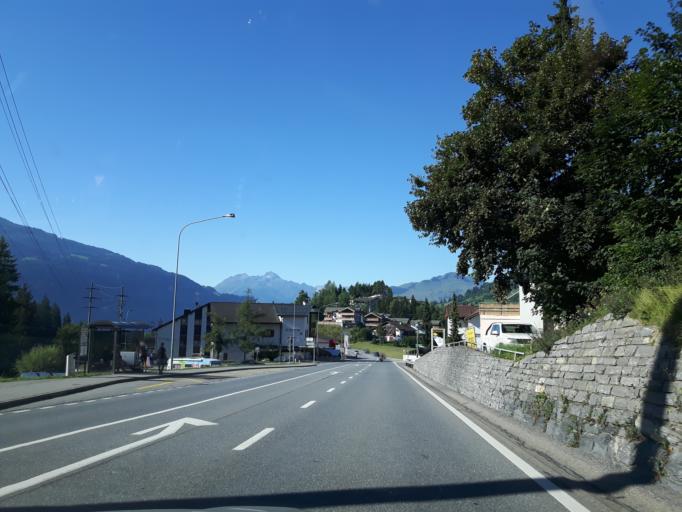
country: CH
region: Grisons
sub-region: Surselva District
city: Laax
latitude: 46.8134
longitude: 9.2641
